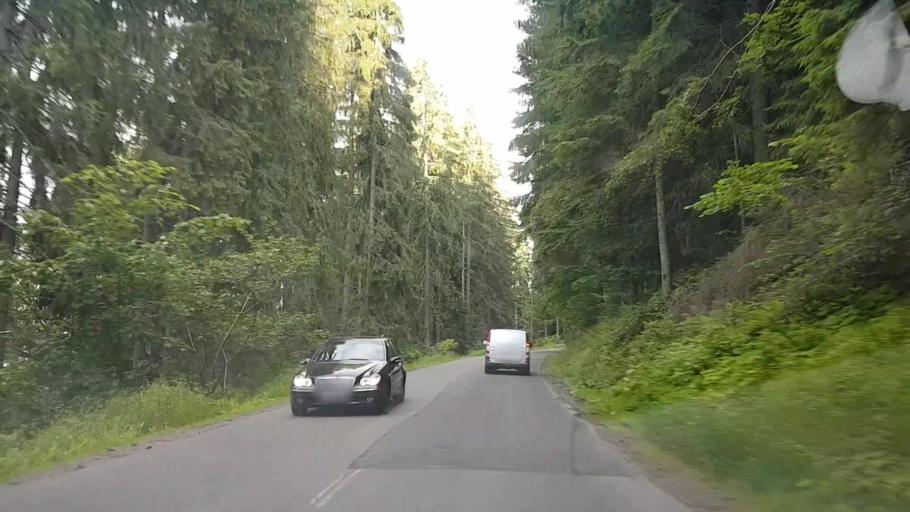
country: RO
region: Harghita
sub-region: Comuna Remetea
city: Remetea
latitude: 46.6725
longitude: 25.3411
